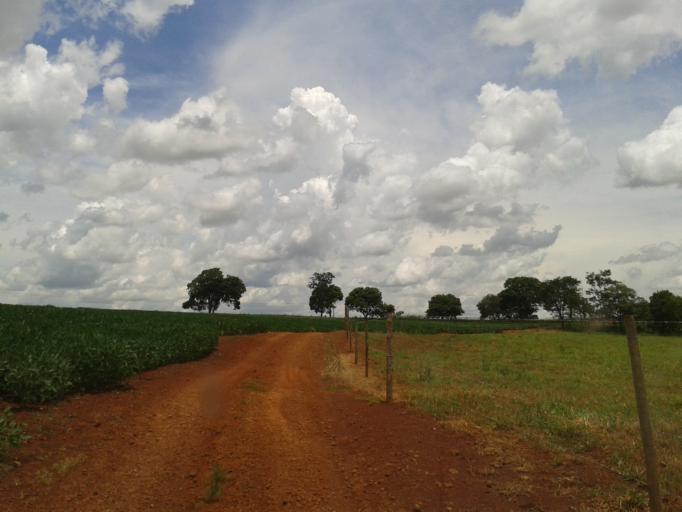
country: BR
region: Minas Gerais
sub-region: Centralina
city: Centralina
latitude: -18.7046
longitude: -49.2183
